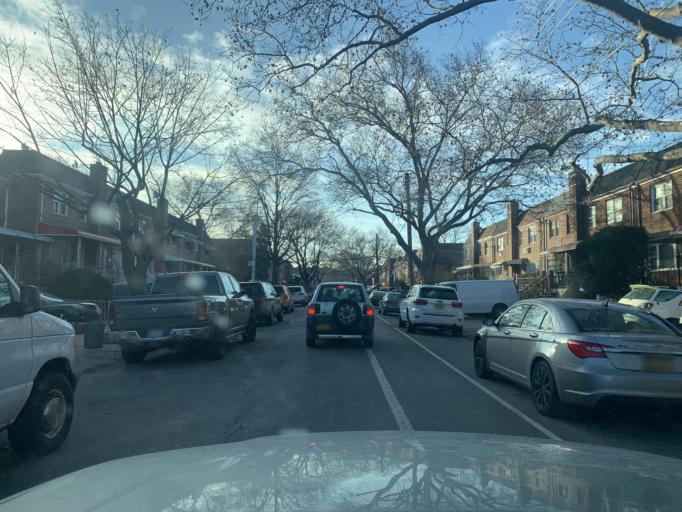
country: US
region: New York
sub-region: Queens County
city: Long Island City
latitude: 40.7578
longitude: -73.8924
